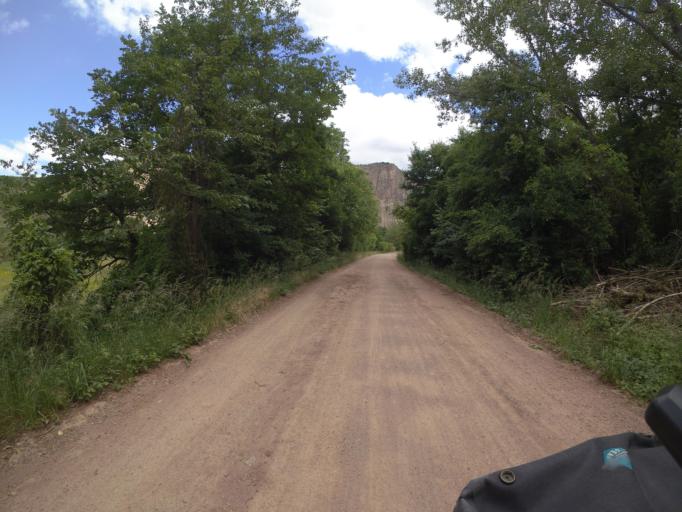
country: DE
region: Rheinland-Pfalz
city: Traisen
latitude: 49.8137
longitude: 7.8246
